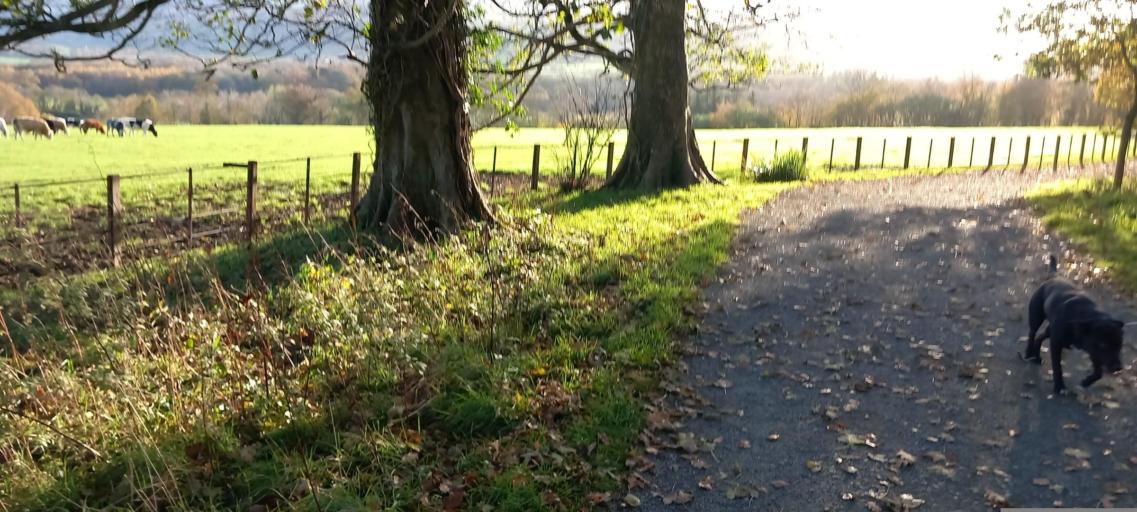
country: GB
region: Wales
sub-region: Anglesey
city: Beaumaris
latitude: 53.2266
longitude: -4.0932
